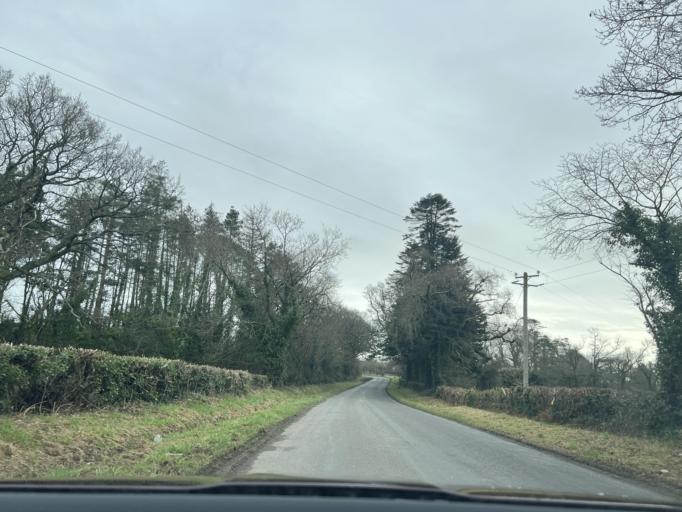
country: IE
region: Leinster
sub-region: Loch Garman
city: Castlebridge
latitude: 52.3838
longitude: -6.5224
